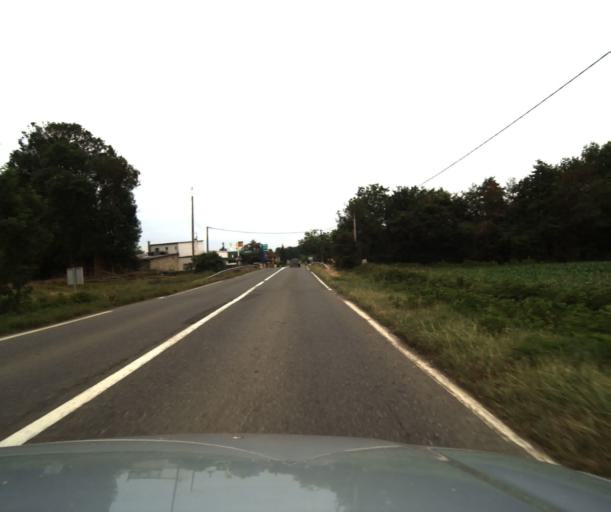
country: FR
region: Midi-Pyrenees
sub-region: Departement du Gers
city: Mielan
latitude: 43.4711
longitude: 0.3297
